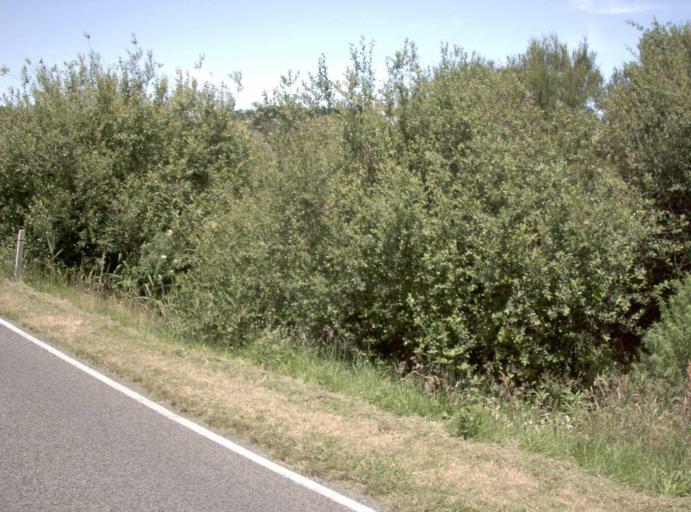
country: AU
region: Victoria
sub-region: Bass Coast
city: North Wonthaggi
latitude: -38.7675
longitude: 146.1561
